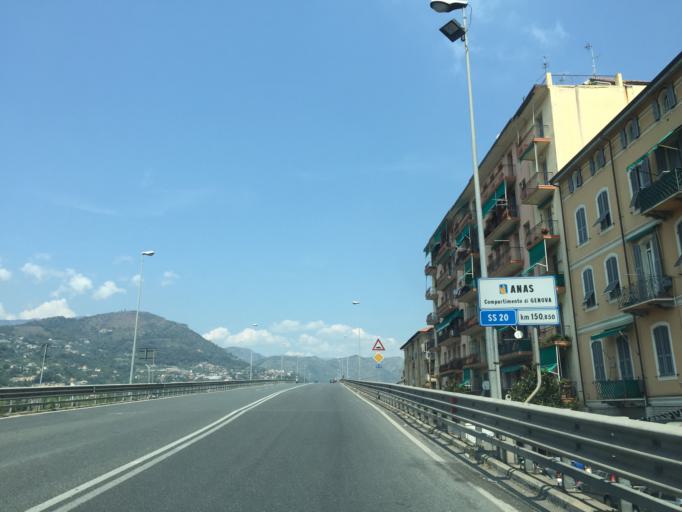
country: IT
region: Liguria
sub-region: Provincia di Imperia
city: Ventimiglia
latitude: 43.7935
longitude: 7.6048
